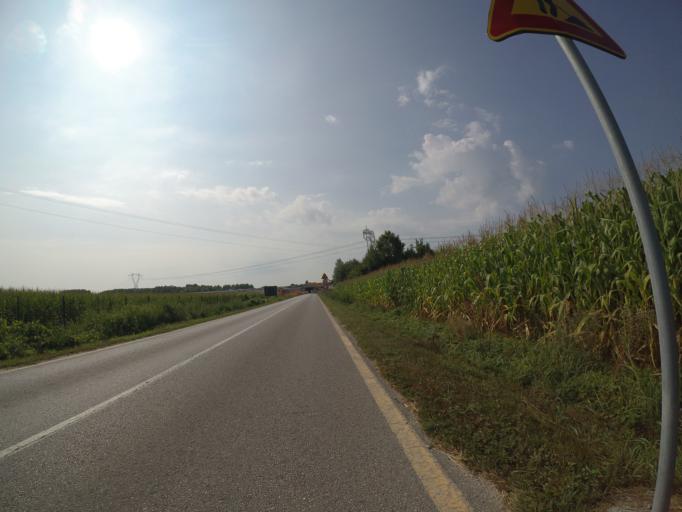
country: IT
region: Friuli Venezia Giulia
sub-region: Provincia di Udine
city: Pocenia
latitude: 45.8302
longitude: 13.0802
